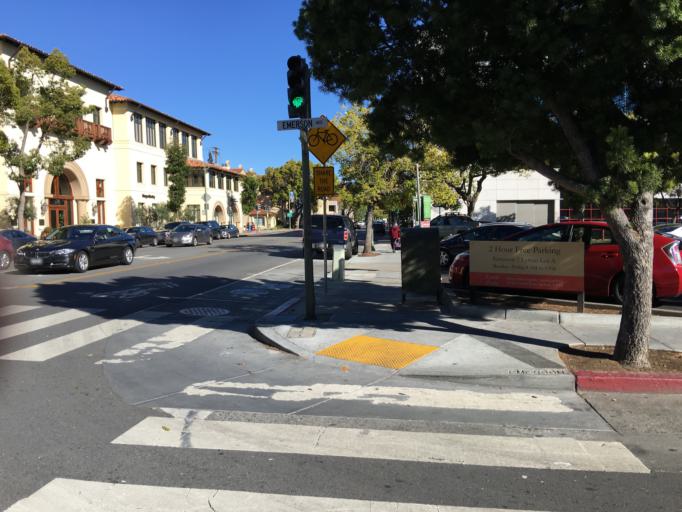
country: US
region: California
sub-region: San Mateo County
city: Menlo Park
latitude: 37.4455
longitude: -122.1640
